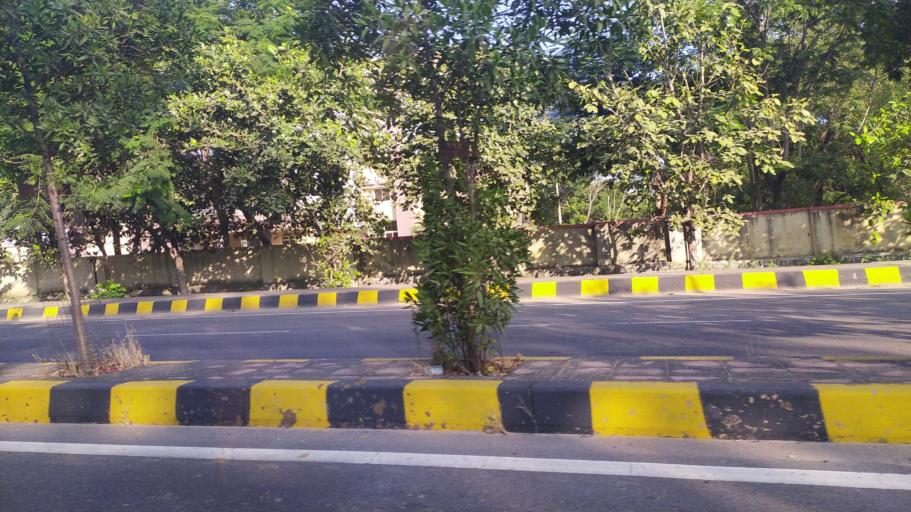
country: IN
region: Telangana
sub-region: Hyderabad
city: Hyderabad
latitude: 17.3206
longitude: 78.3971
